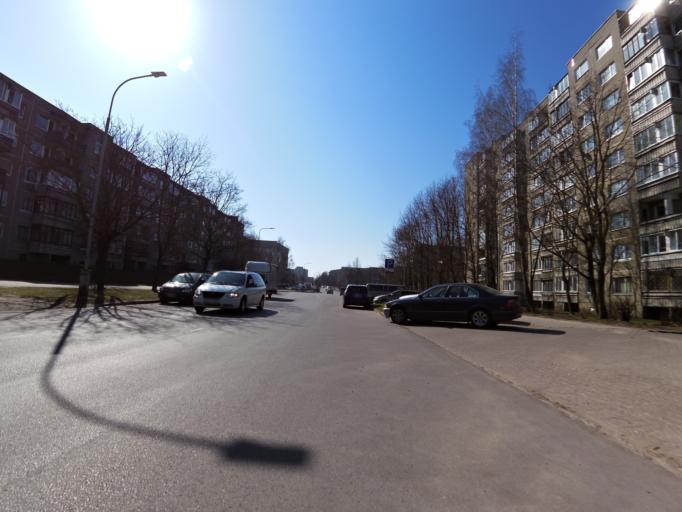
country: LT
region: Vilnius County
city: Justiniskes
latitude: 54.7200
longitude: 25.2140
